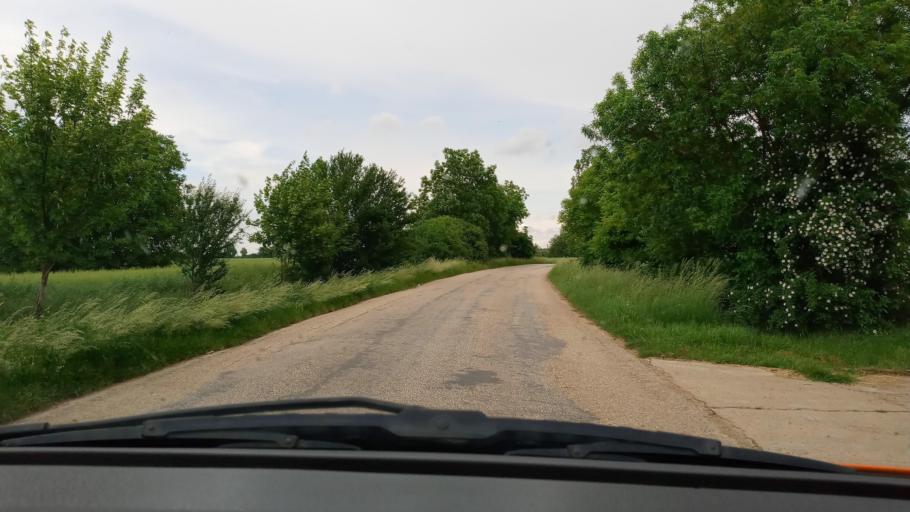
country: HU
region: Baranya
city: Harkany
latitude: 45.9182
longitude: 18.1581
